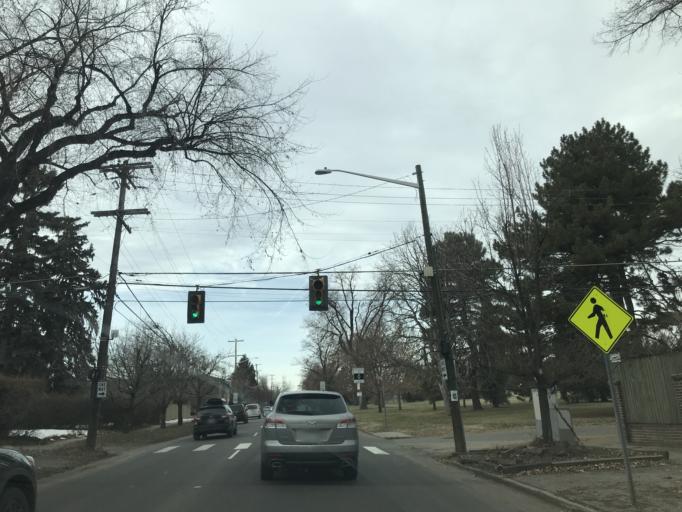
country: US
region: Colorado
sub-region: Denver County
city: Denver
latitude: 39.7292
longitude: -104.9544
